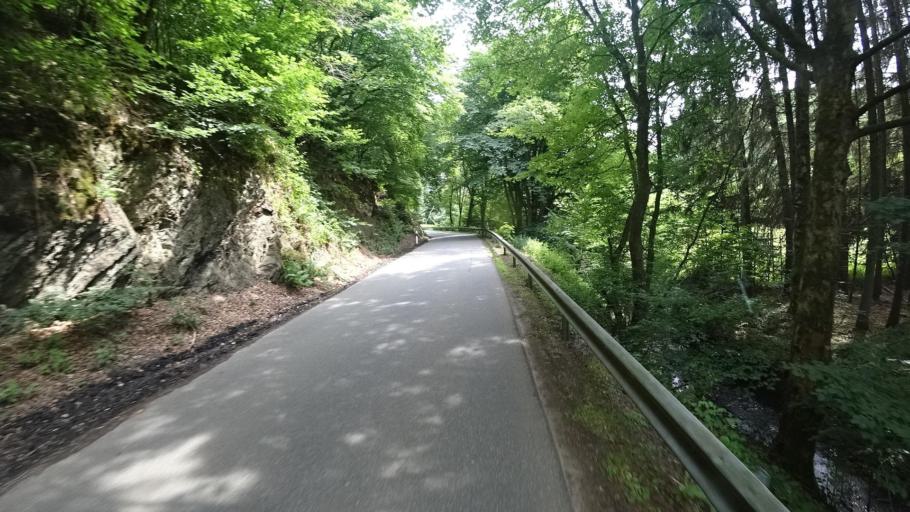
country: DE
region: Rheinland-Pfalz
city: Walterschen
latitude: 50.6751
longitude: 7.5722
